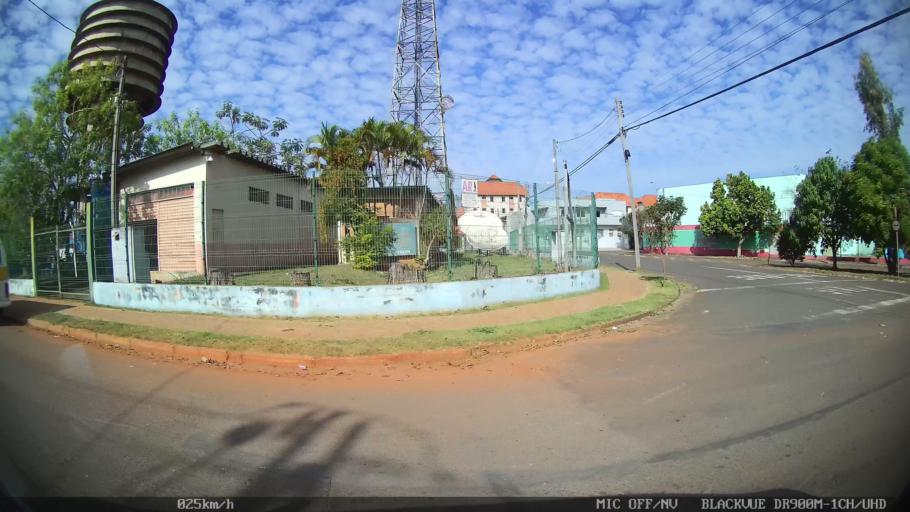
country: BR
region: Sao Paulo
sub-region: Santa Barbara D'Oeste
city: Santa Barbara d'Oeste
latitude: -22.7630
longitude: -47.3981
